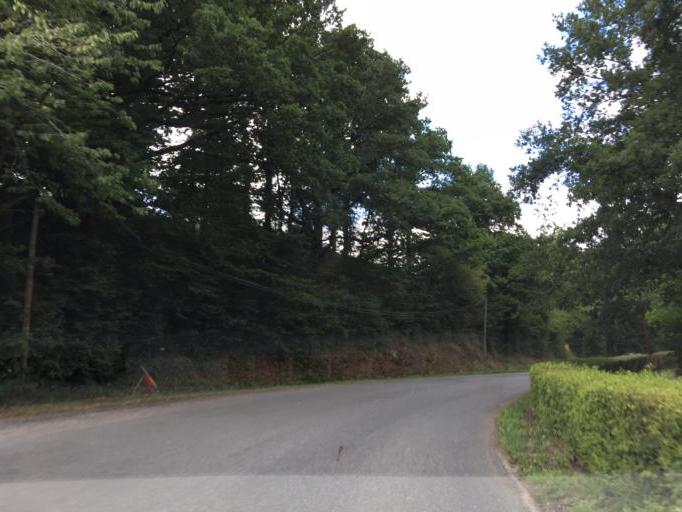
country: FR
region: Midi-Pyrenees
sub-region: Departement de l'Aveyron
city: Pont-de-Salars
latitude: 44.2871
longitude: 2.7266
